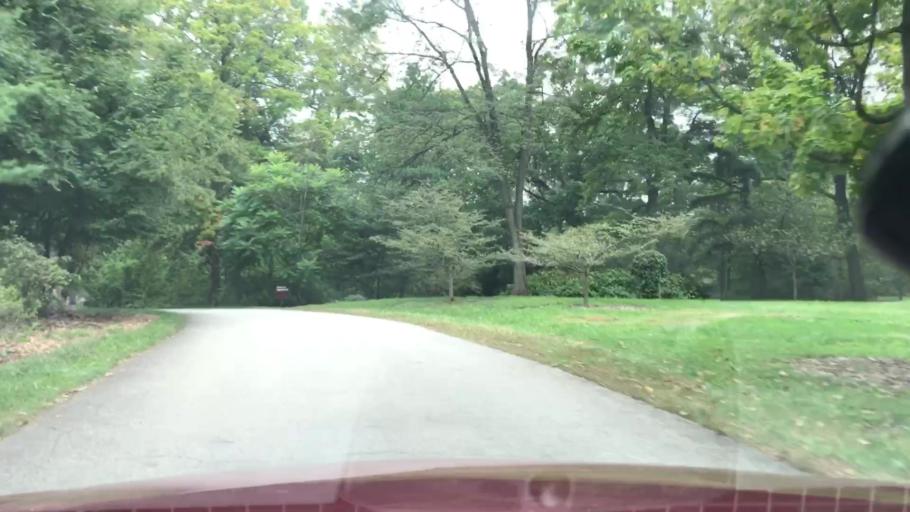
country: US
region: Illinois
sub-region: DuPage County
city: Lisle
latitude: 41.8185
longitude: -88.0605
